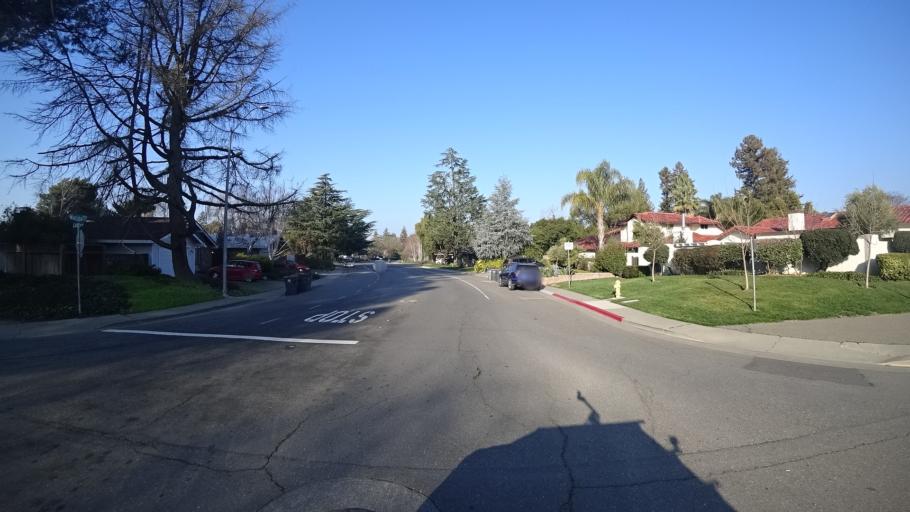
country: US
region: California
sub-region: Yolo County
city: Davis
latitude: 38.5486
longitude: -121.7891
